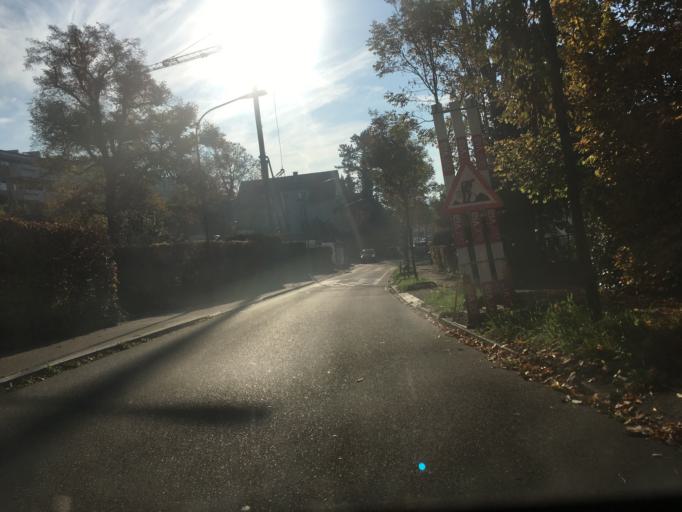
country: CH
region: Zurich
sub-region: Bezirk Zuerich
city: Zuerich (Kreis 10) / Hoengg
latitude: 47.3993
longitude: 8.5037
